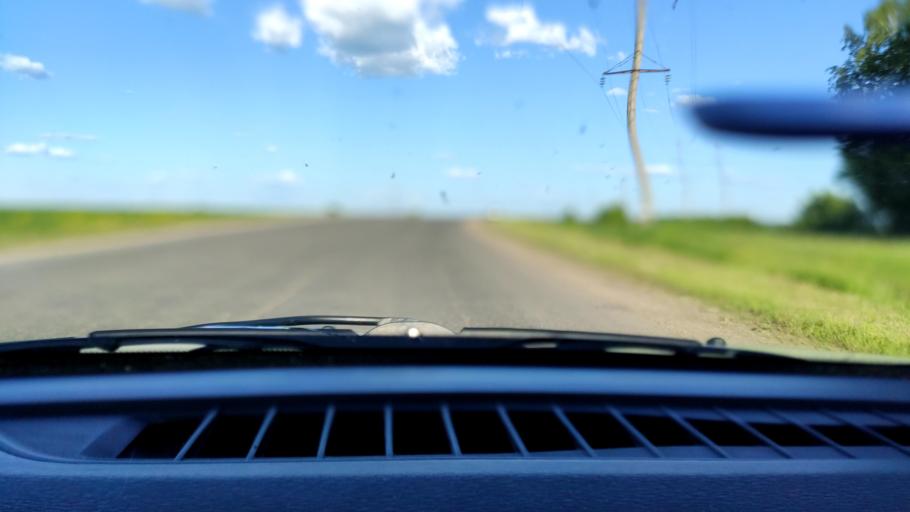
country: RU
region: Perm
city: Orda
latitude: 57.1906
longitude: 56.8633
